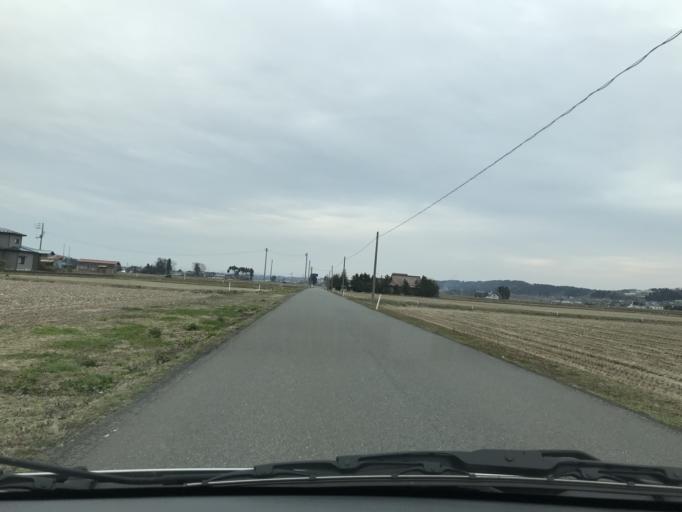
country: JP
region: Iwate
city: Mizusawa
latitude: 39.0799
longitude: 141.1432
